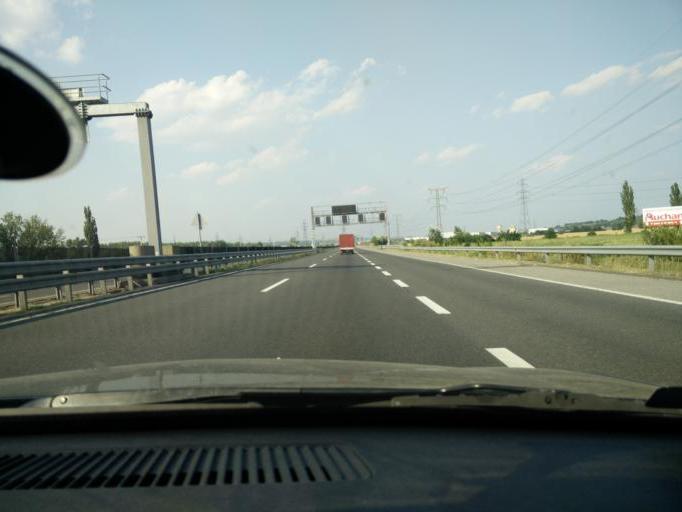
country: HU
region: Pest
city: Diosd
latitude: 47.3752
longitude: 18.9462
